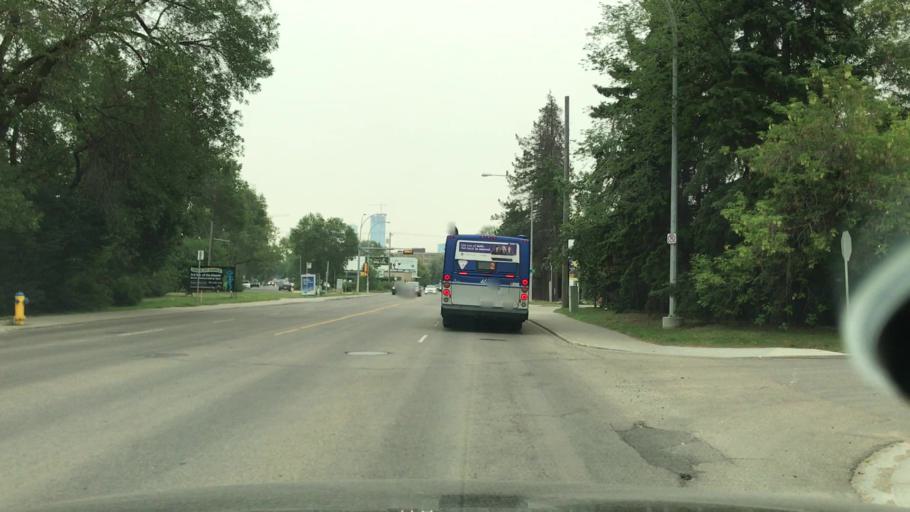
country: CA
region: Alberta
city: Edmonton
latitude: 53.5478
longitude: -113.5430
